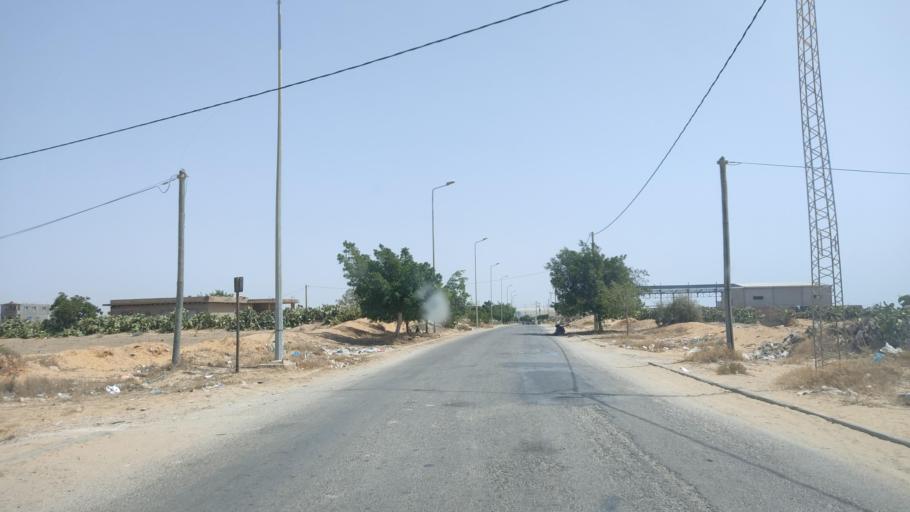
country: TN
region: Safaqis
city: Sfax
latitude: 34.6777
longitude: 10.7185
